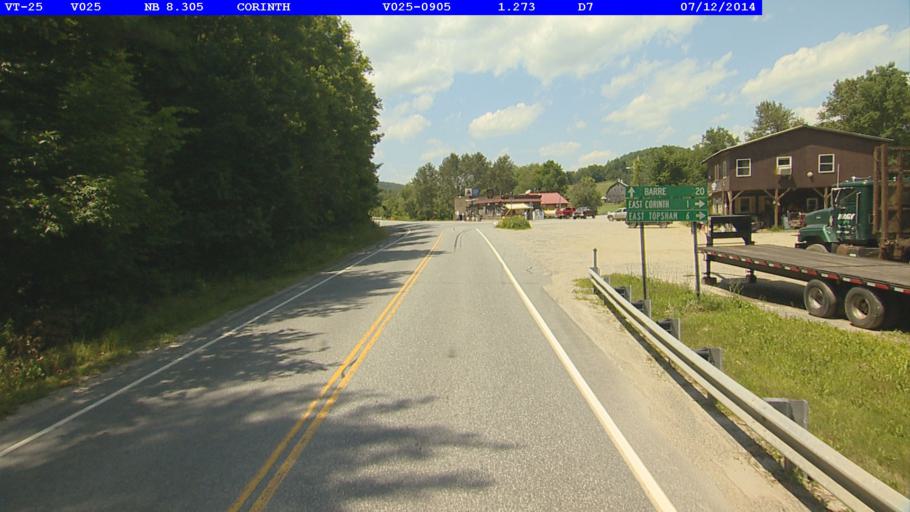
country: US
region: New Hampshire
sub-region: Grafton County
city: Haverhill
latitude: 44.0543
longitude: -72.2201
